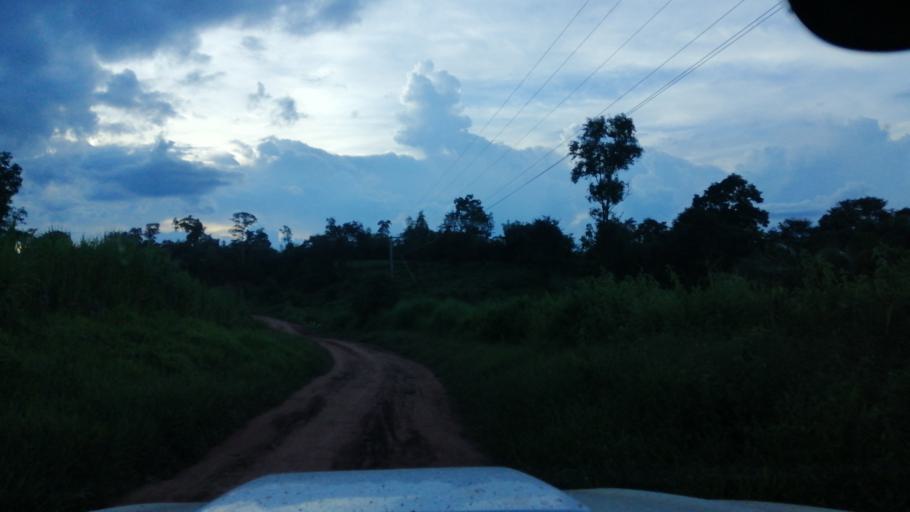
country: TH
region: Uttaradit
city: Ban Khok
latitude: 17.8762
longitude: 101.0791
